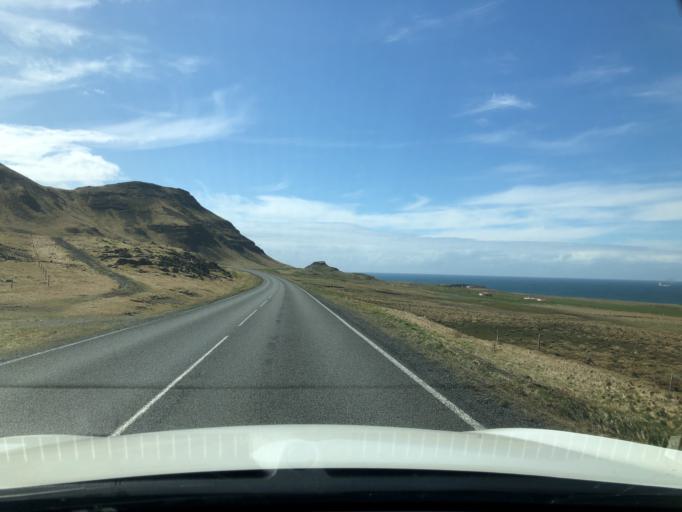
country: IS
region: Capital Region
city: Mosfellsbaer
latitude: 64.2890
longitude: -21.8065
